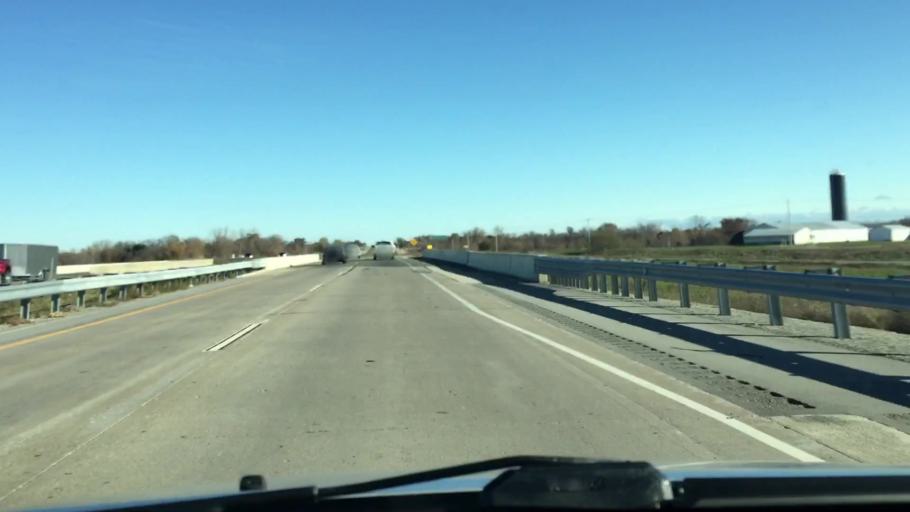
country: US
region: Wisconsin
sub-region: Brown County
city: Wrightstown
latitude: 44.3489
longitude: -88.1936
